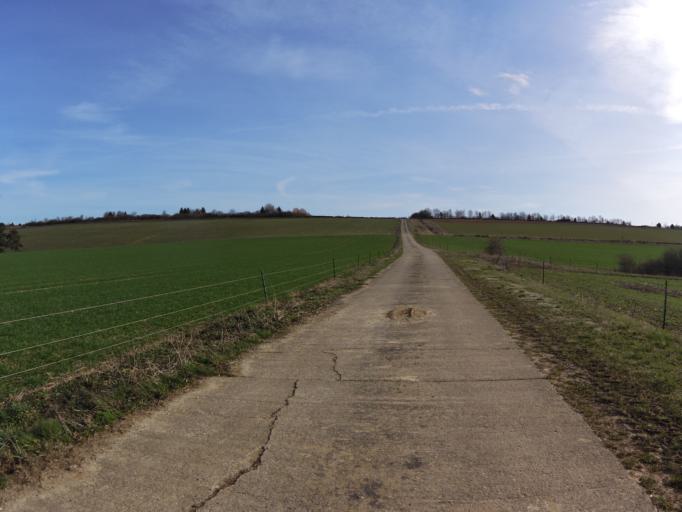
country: DE
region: Bavaria
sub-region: Regierungsbezirk Unterfranken
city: Greussenheim
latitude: 49.8334
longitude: 9.7971
